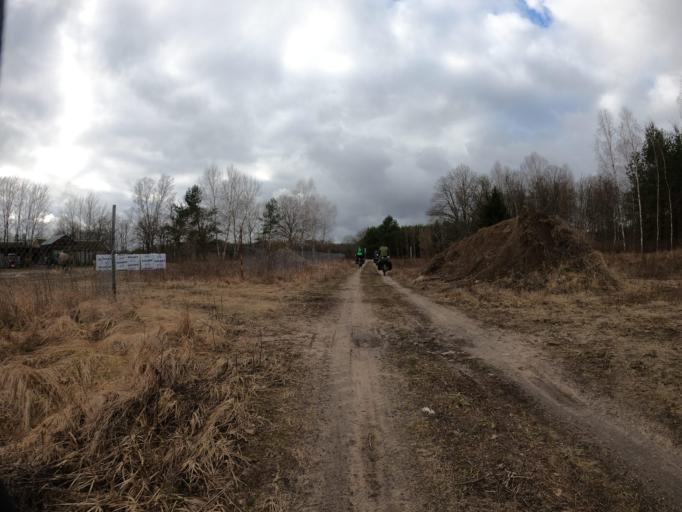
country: PL
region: Greater Poland Voivodeship
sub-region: Powiat zlotowski
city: Sypniewo
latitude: 53.4718
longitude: 16.4974
